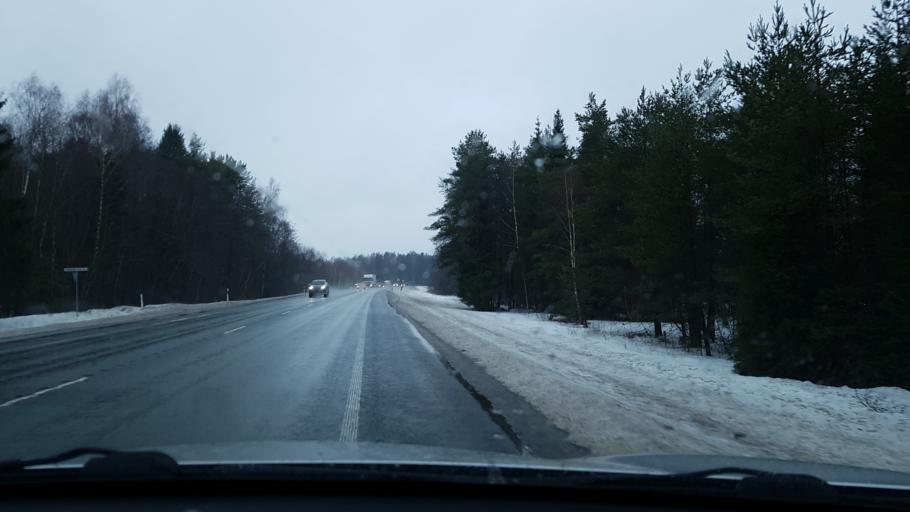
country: EE
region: Raplamaa
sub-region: Kohila vald
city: Kohila
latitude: 59.1589
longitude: 24.7749
